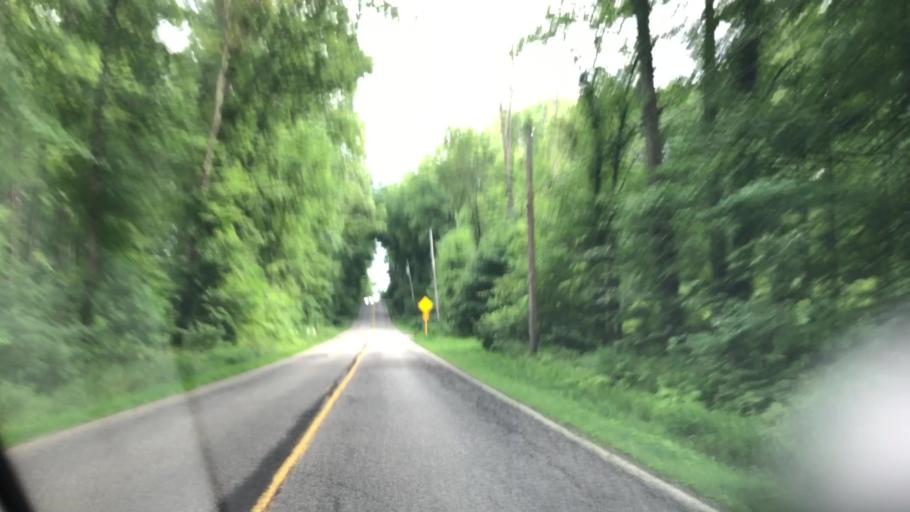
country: US
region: Ohio
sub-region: Summit County
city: Montrose-Ghent
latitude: 41.1262
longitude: -81.7159
